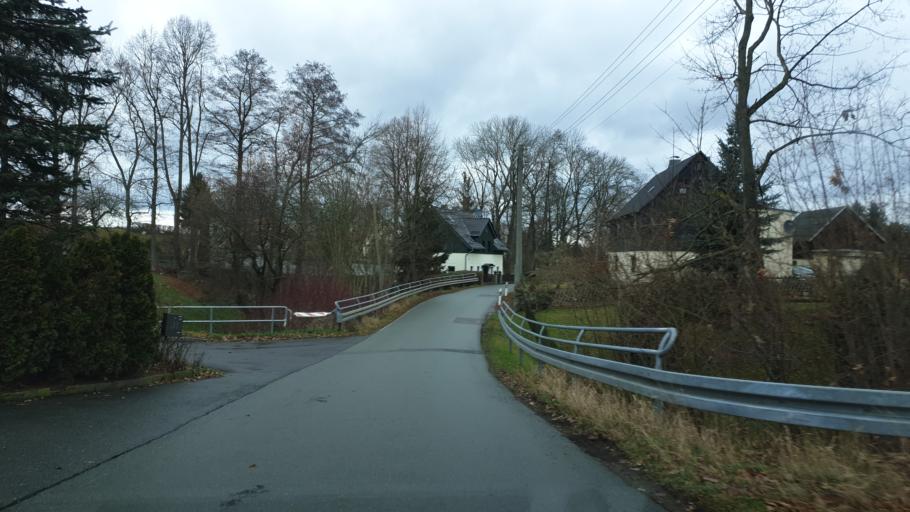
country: DE
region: Saxony
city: Bernsdorf
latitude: 50.7593
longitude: 12.6668
